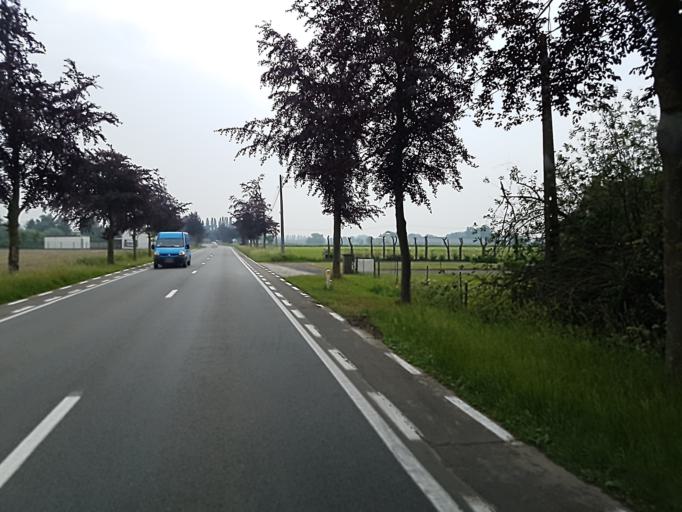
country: BE
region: Flanders
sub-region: Provincie West-Vlaanderen
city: Dentergem
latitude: 50.9537
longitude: 3.3737
